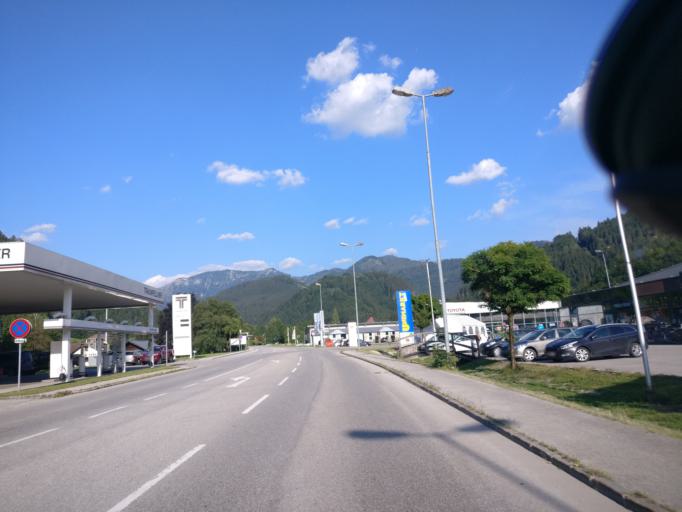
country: AT
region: Lower Austria
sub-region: Politischer Bezirk Scheibbs
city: Gostling an der Ybbs
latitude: 47.8073
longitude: 14.9368
